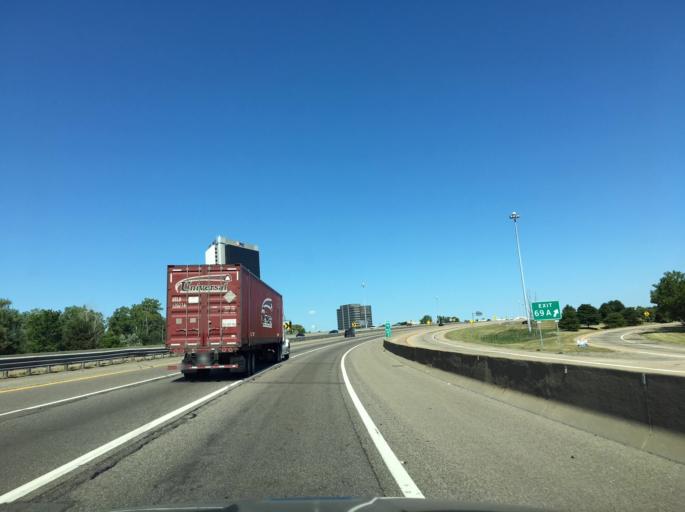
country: US
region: Michigan
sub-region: Oakland County
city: Clawson
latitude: 42.5593
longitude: -83.1536
